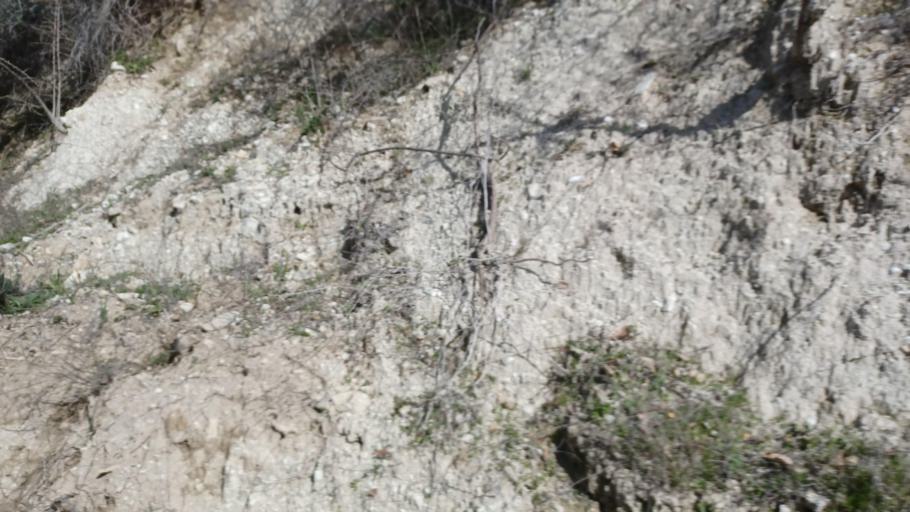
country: CY
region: Limassol
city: Pachna
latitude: 34.8429
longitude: 32.7235
